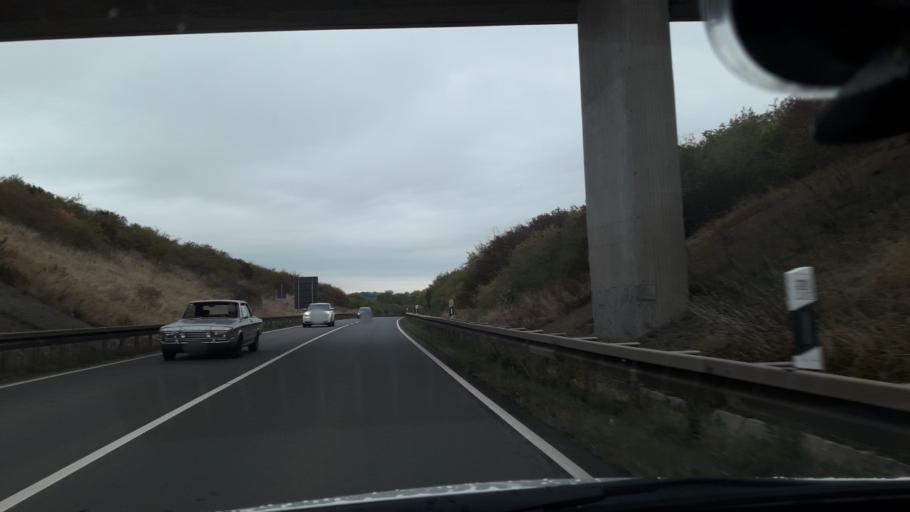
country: DE
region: Lower Saxony
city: Schladen
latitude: 52.0282
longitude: 10.5371
